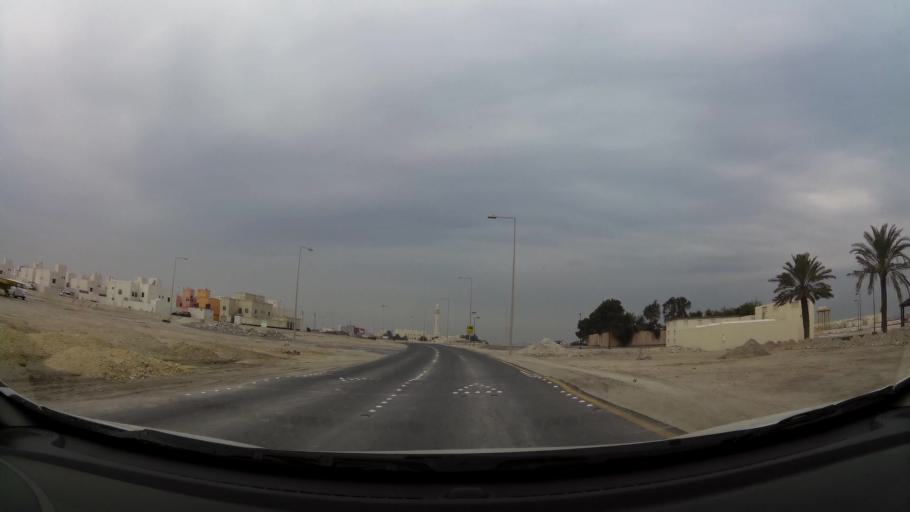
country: BH
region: Northern
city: Ar Rifa'
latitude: 26.0501
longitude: 50.6202
